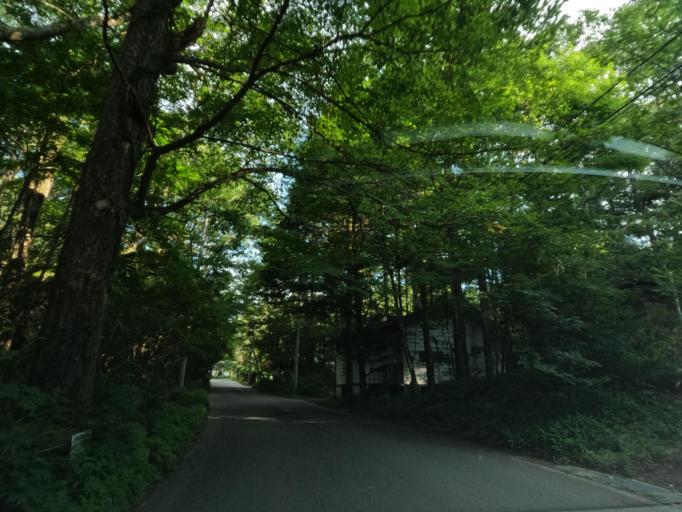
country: JP
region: Nagano
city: Komoro
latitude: 36.4545
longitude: 138.5693
